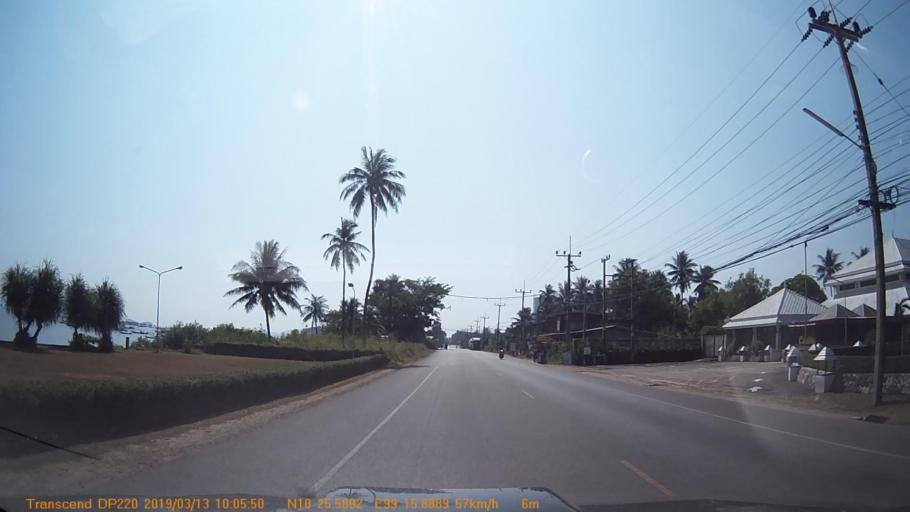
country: TH
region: Chumphon
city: Chumphon
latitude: 10.4263
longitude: 99.2651
